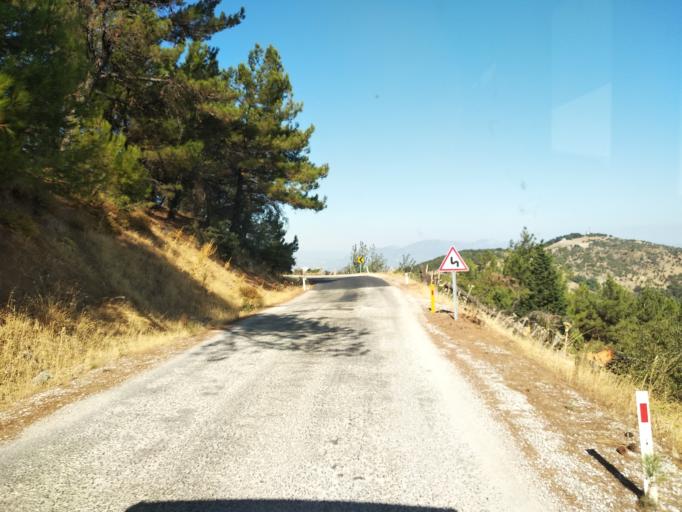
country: TR
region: Izmir
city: Gaziemir
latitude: 38.3137
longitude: 27.0051
